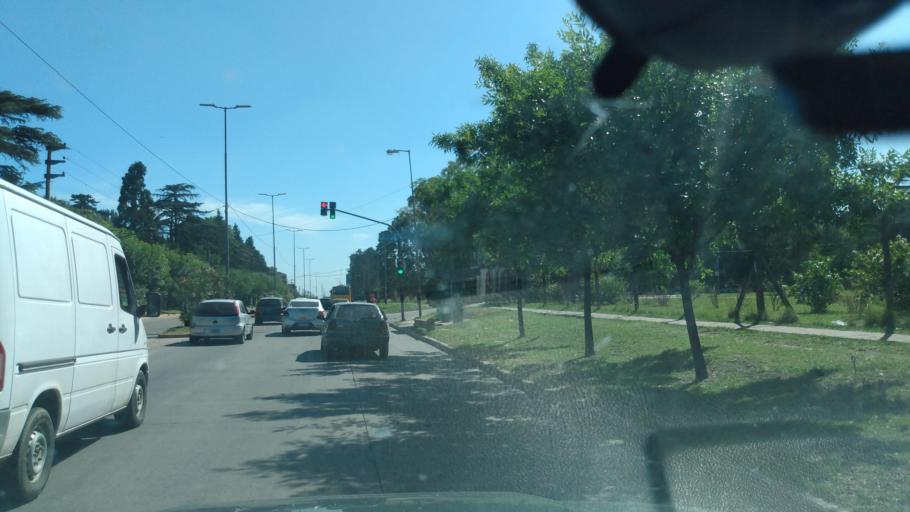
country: AR
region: Buenos Aires
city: Hurlingham
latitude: -34.5582
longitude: -58.7294
